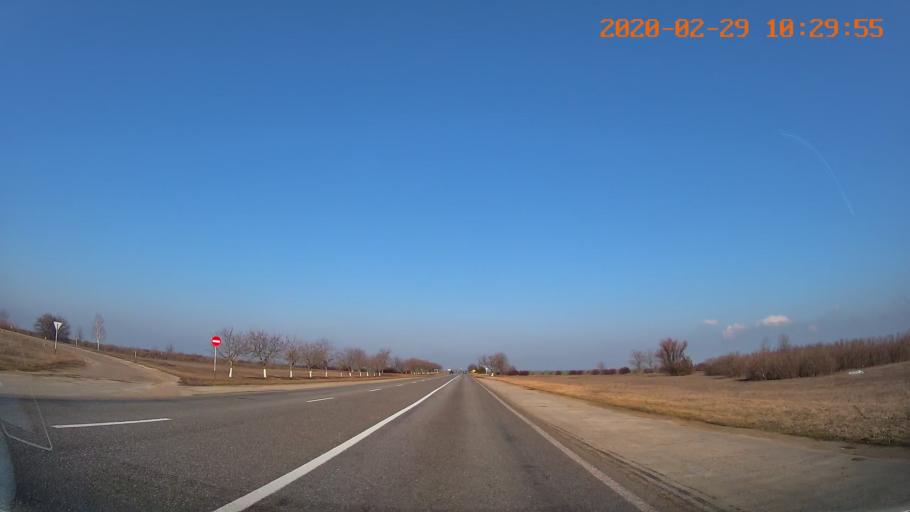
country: MD
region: Telenesti
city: Tiraspolul Nou
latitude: 46.9293
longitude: 29.5809
